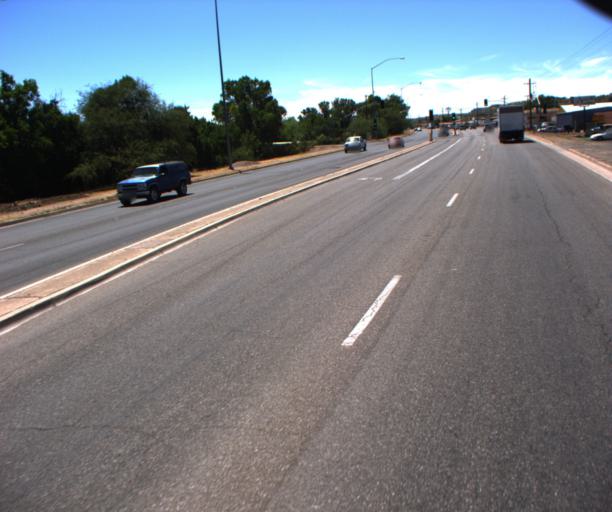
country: US
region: Arizona
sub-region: Santa Cruz County
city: Nogales
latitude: 31.3844
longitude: -110.9484
